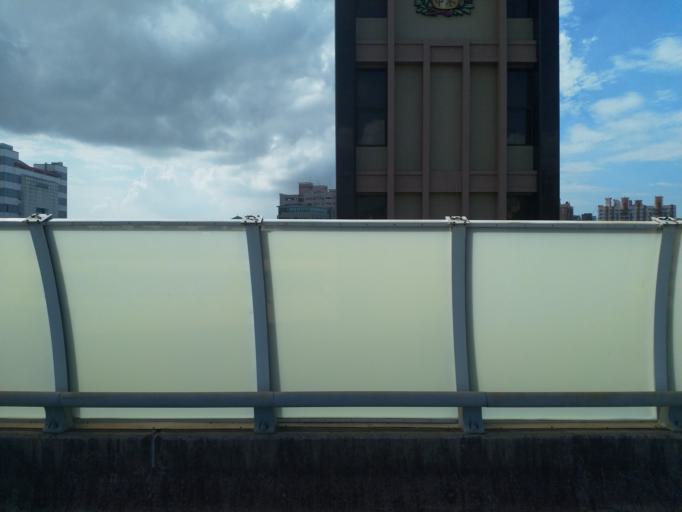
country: TW
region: Kaohsiung
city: Kaohsiung
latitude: 22.6789
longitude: 120.3153
